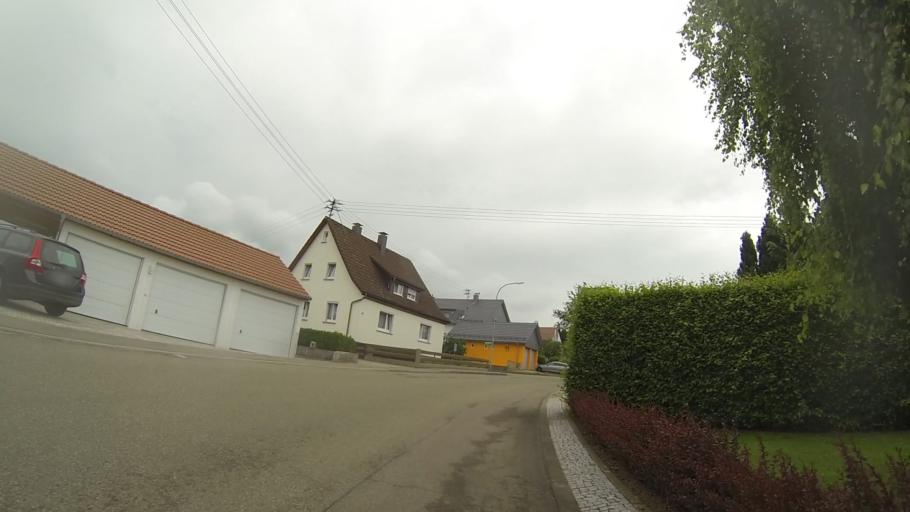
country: DE
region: Baden-Wuerttemberg
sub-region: Regierungsbezirk Stuttgart
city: Steinheim am Albuch
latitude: 48.6890
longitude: 10.0681
